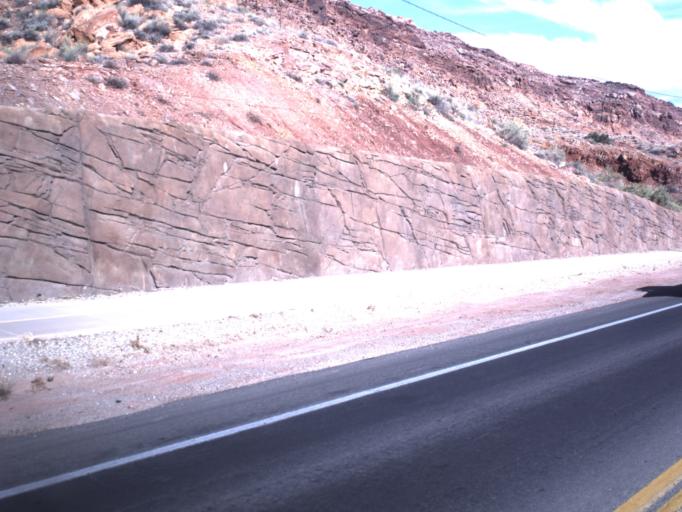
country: US
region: Utah
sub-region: Grand County
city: Moab
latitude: 38.5975
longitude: -109.5716
